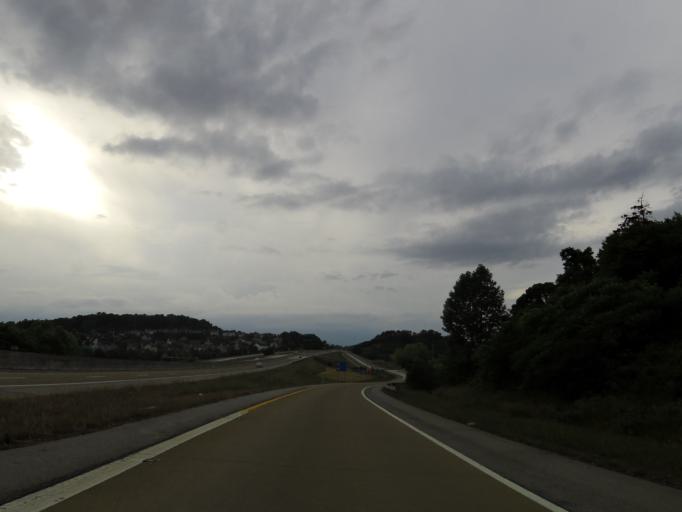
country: US
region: Tennessee
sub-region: Knox County
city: Farragut
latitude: 35.8740
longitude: -84.0919
